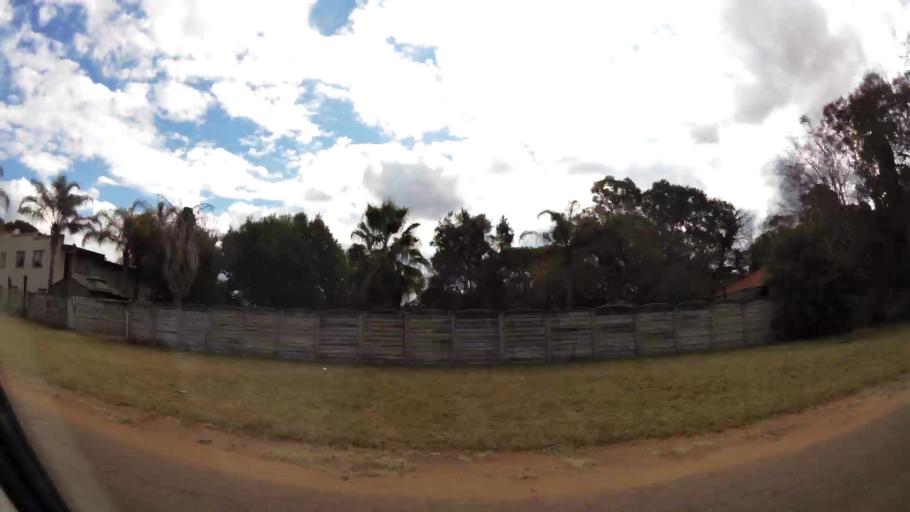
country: ZA
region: Limpopo
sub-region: Waterberg District Municipality
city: Modimolle
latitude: -24.7103
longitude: 28.4041
